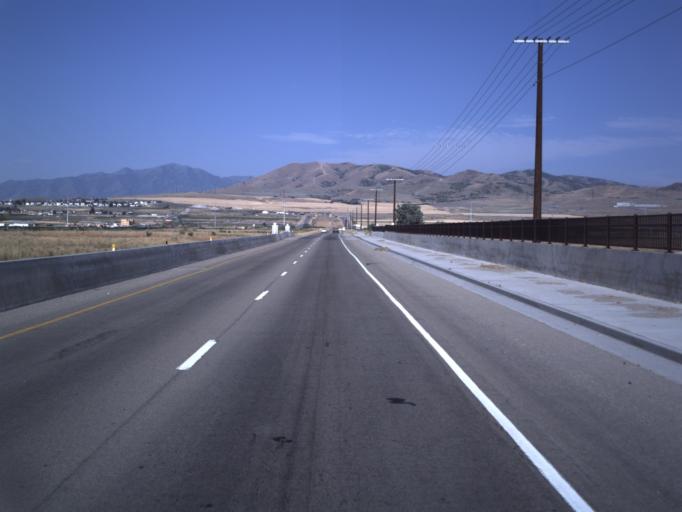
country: US
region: Utah
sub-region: Utah County
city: Lehi
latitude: 40.4132
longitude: -111.8943
